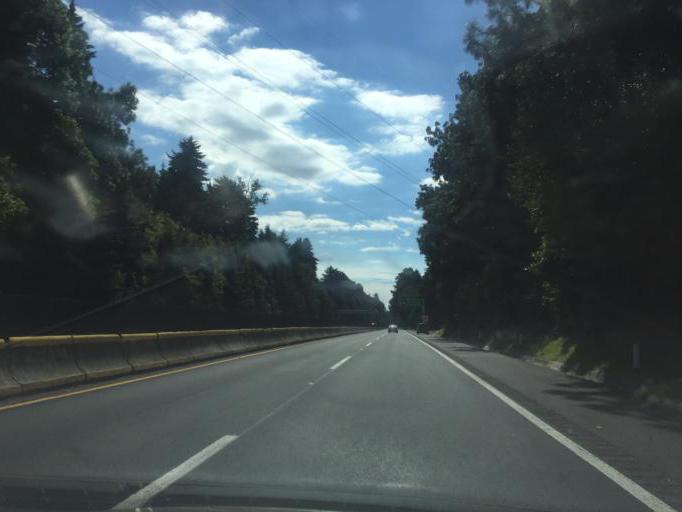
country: MX
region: Morelos
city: Tres Marias
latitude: 19.0463
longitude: -99.2363
